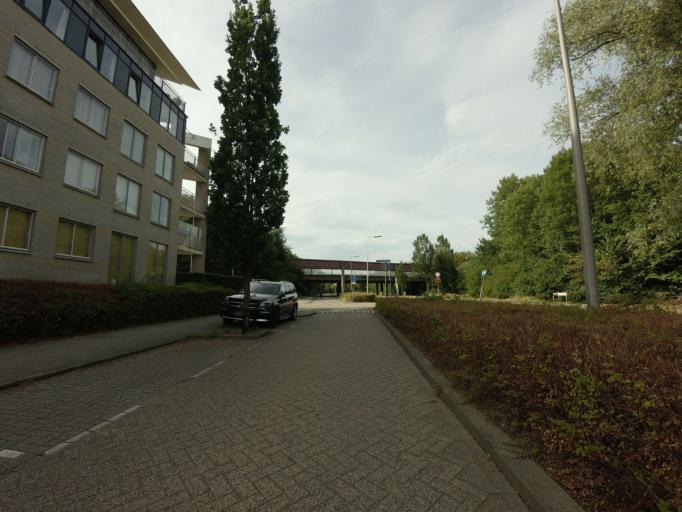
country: NL
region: Utrecht
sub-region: Gemeente Utrecht
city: Lunetten
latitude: 52.0681
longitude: 5.1304
